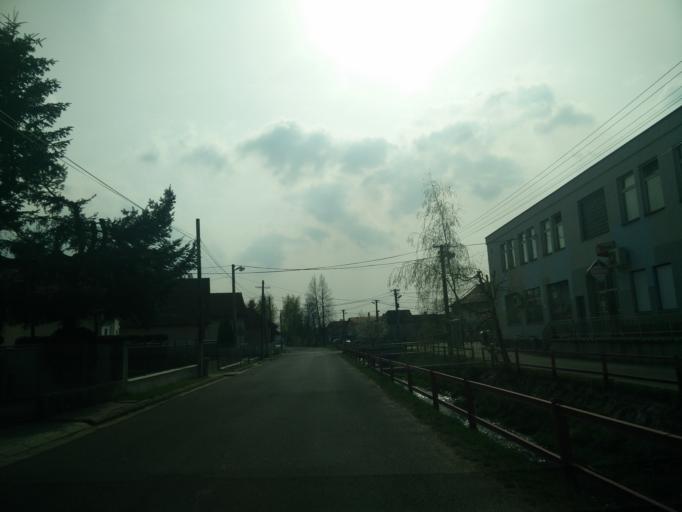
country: SK
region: Nitriansky
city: Prievidza
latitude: 48.8176
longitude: 18.6515
